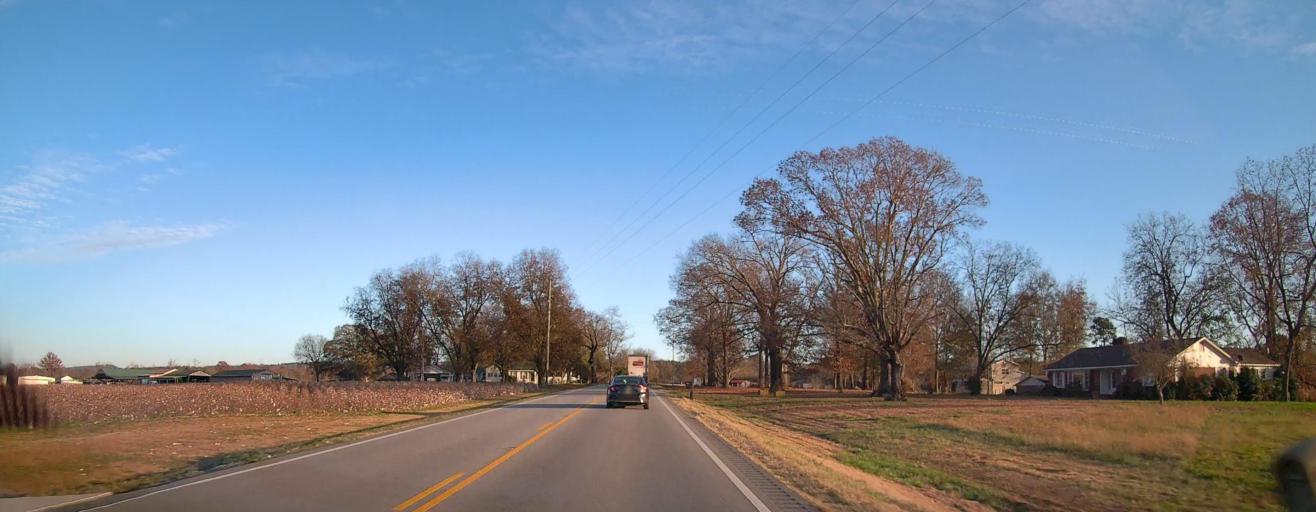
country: US
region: Alabama
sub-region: Blount County
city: Oneonta
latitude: 34.0962
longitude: -86.3588
